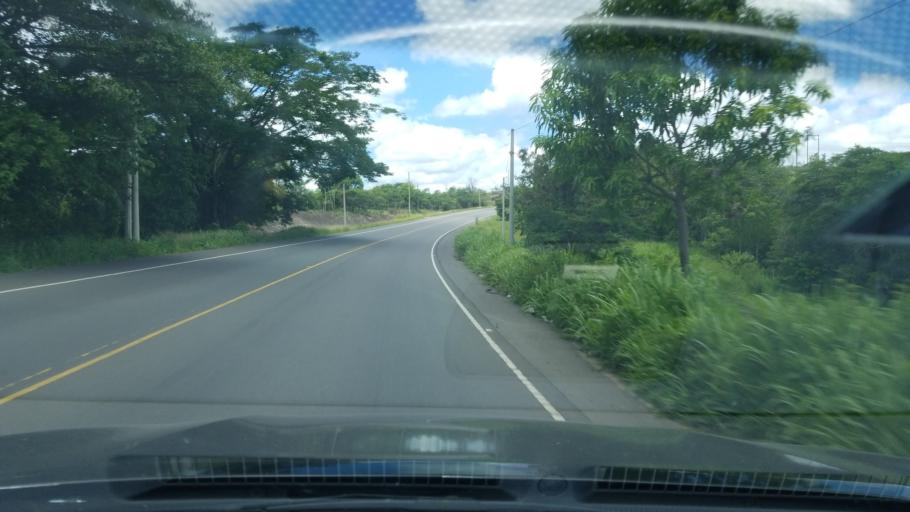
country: HN
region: Francisco Morazan
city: Cofradia
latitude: 14.3085
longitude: -87.2185
